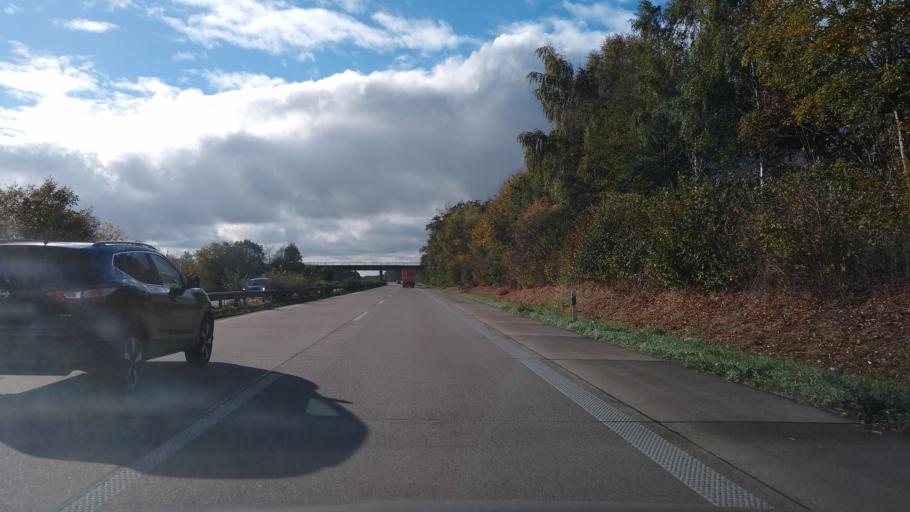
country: DE
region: Lower Saxony
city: Grossenkneten
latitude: 52.9820
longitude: 8.1920
